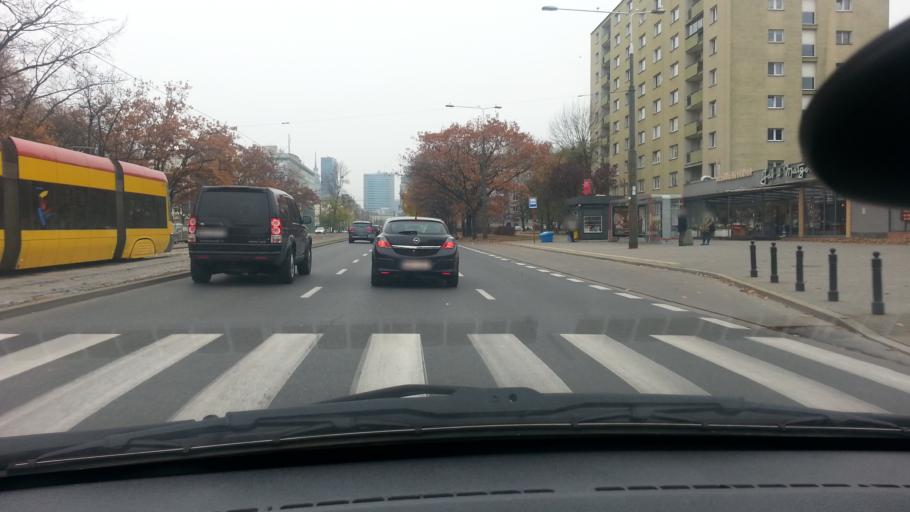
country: PL
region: Masovian Voivodeship
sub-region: Warszawa
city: Wola
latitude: 52.2472
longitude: 20.9888
